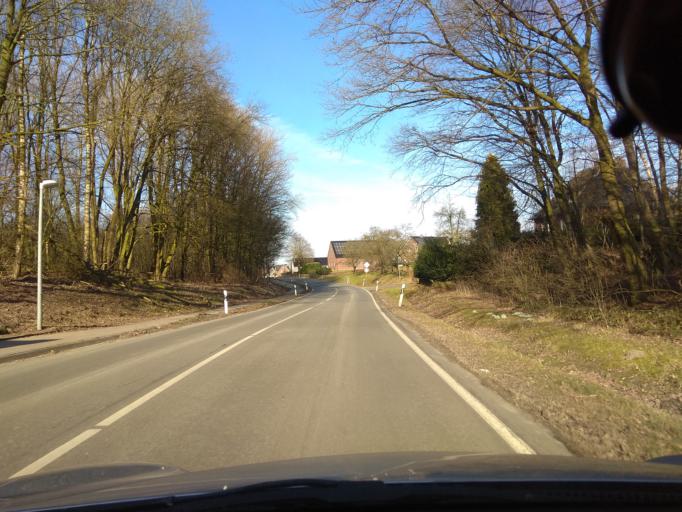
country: DE
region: North Rhine-Westphalia
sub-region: Regierungsbezirk Munster
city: Mettingen
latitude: 52.2963
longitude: 7.7751
